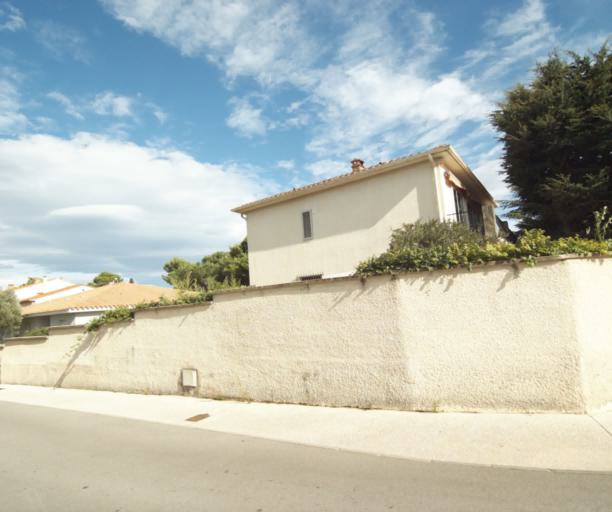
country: FR
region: Languedoc-Roussillon
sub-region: Departement des Pyrenees-Orientales
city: Argelers
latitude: 42.5458
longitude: 3.0115
